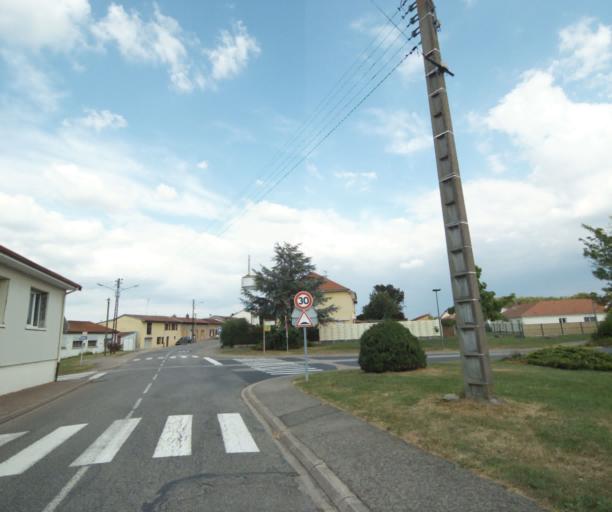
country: FR
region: Lorraine
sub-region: Departement de Meurthe-et-Moselle
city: Chanteheux
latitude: 48.5729
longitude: 6.5324
